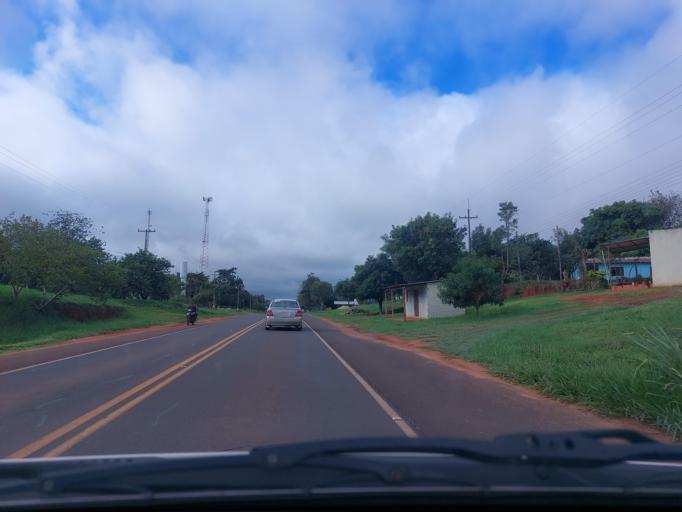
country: PY
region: San Pedro
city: Guayaybi
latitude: -24.5893
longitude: -56.3975
